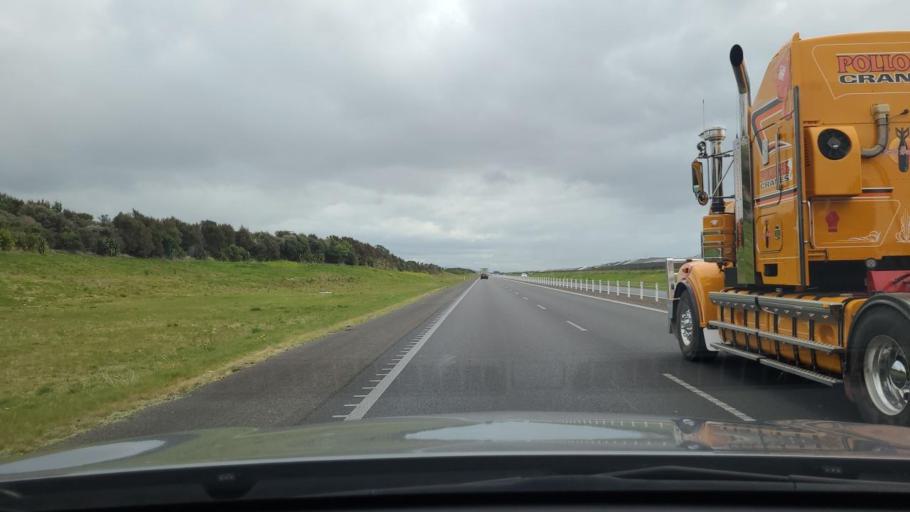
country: NZ
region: Bay of Plenty
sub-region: Western Bay of Plenty District
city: Maketu
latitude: -37.7325
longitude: 176.3434
